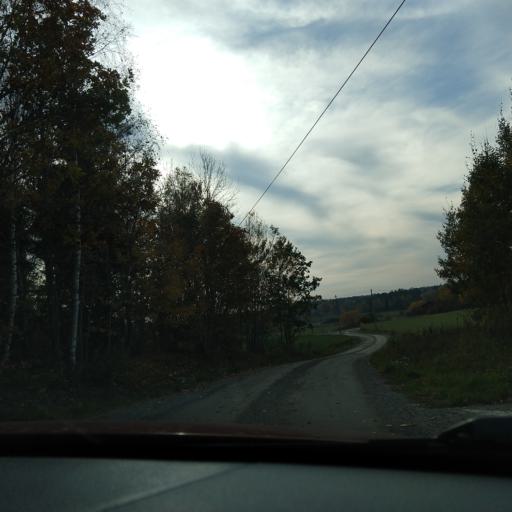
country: SE
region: Stockholm
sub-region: Vallentuna Kommun
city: Vallentuna
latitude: 59.5313
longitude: 18.0083
